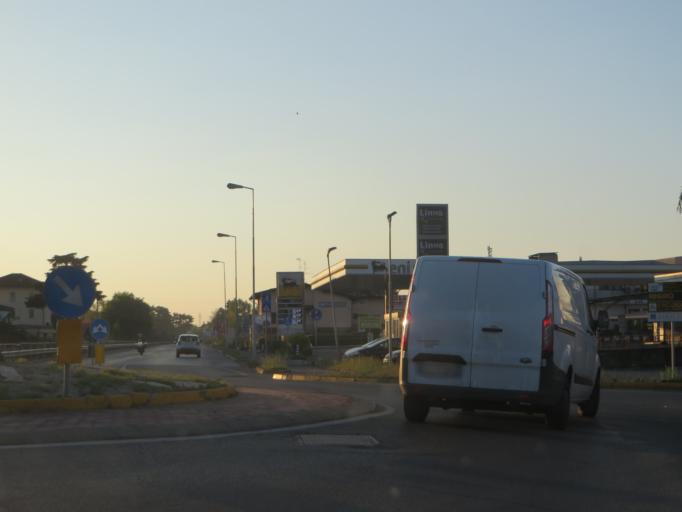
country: IT
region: Lombardy
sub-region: Provincia di Brescia
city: Rezzato
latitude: 45.5098
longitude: 10.3211
